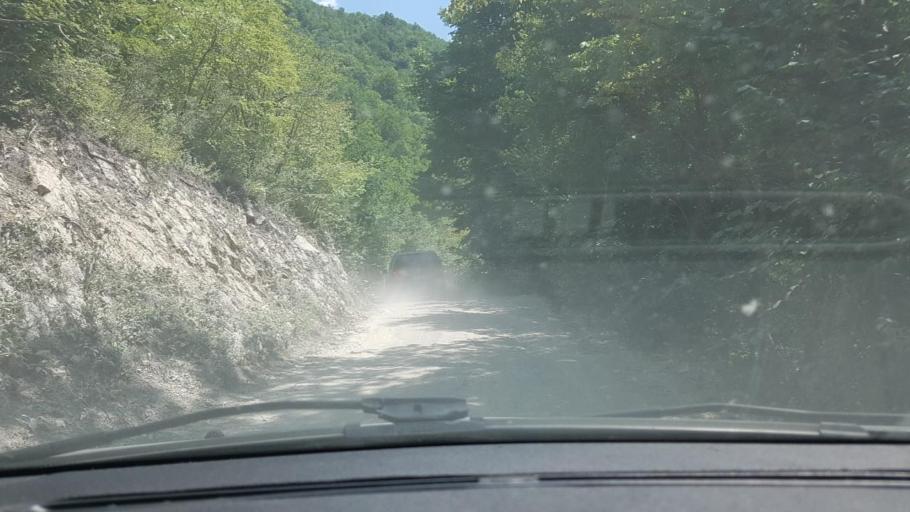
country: BA
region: Federation of Bosnia and Herzegovina
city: Orasac
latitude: 44.6545
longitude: 16.0308
